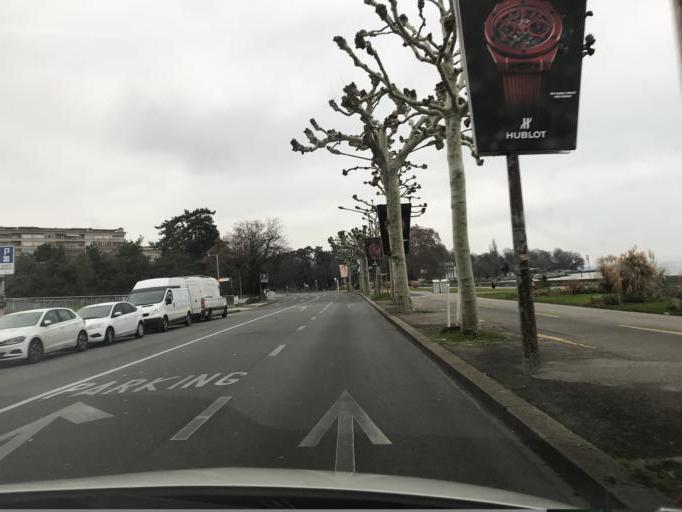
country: CH
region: Geneva
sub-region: Geneva
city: Geneve
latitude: 46.2150
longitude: 6.1519
